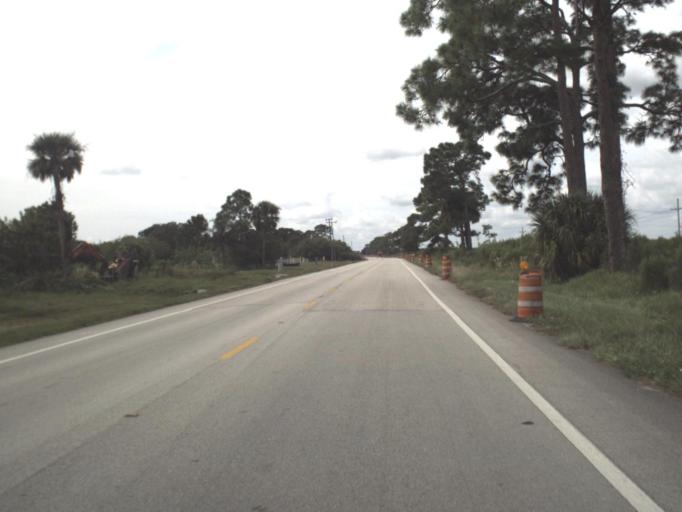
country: US
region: Florida
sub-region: Okeechobee County
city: Taylor Creek
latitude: 27.2751
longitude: -80.7209
